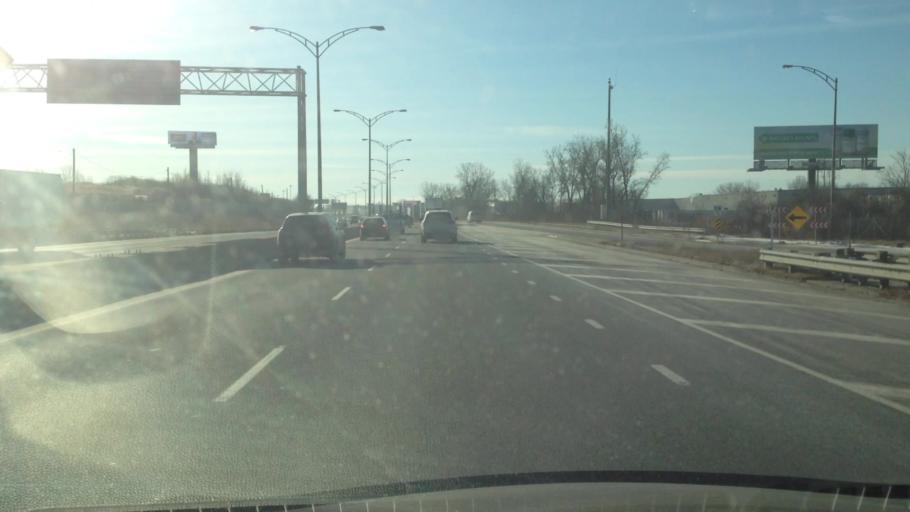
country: CA
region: Quebec
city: Cote-Saint-Luc
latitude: 45.4599
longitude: -73.6968
